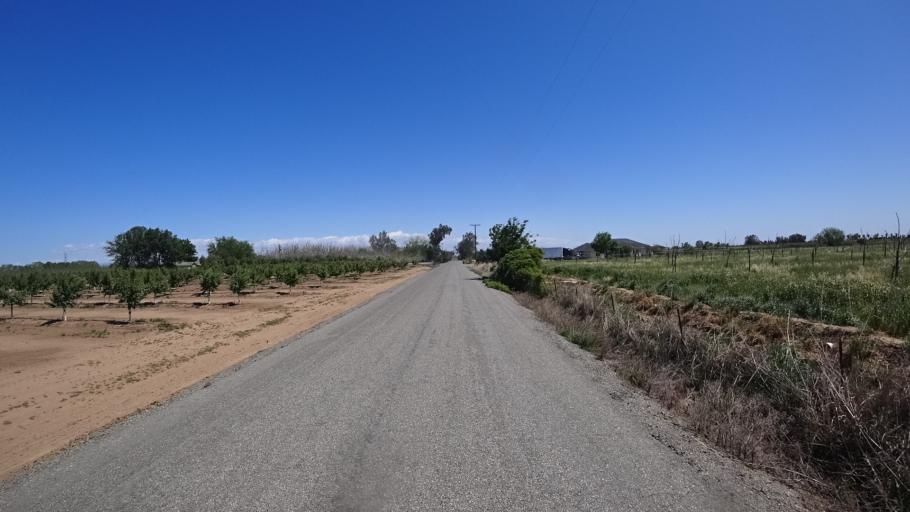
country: US
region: California
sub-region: Glenn County
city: Orland
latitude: 39.7944
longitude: -122.1945
